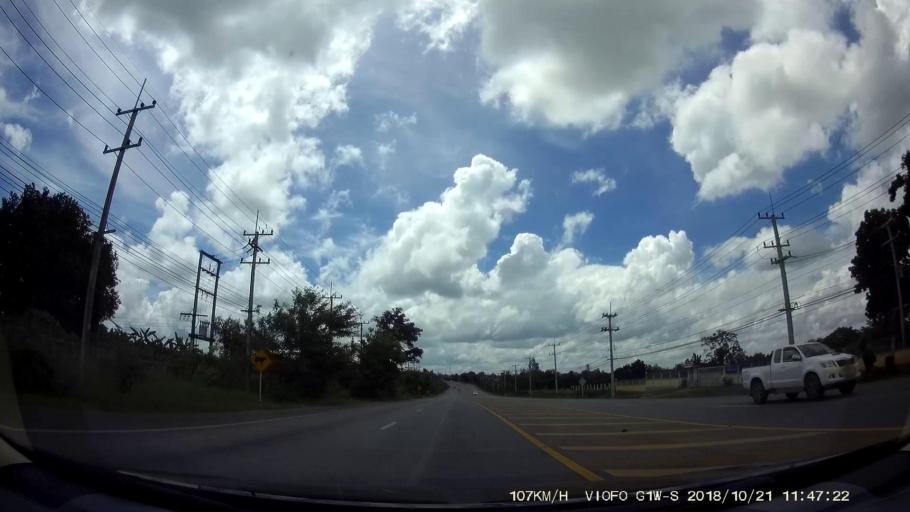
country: TH
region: Chaiyaphum
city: Noen Sa-nga
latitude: 15.6623
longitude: 101.9546
